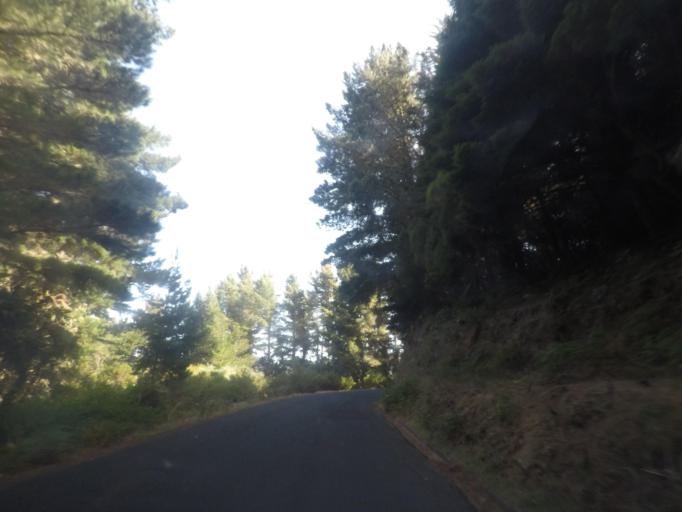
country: PT
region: Madeira
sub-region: Santa Cruz
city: Camacha
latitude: 32.7080
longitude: -16.8782
